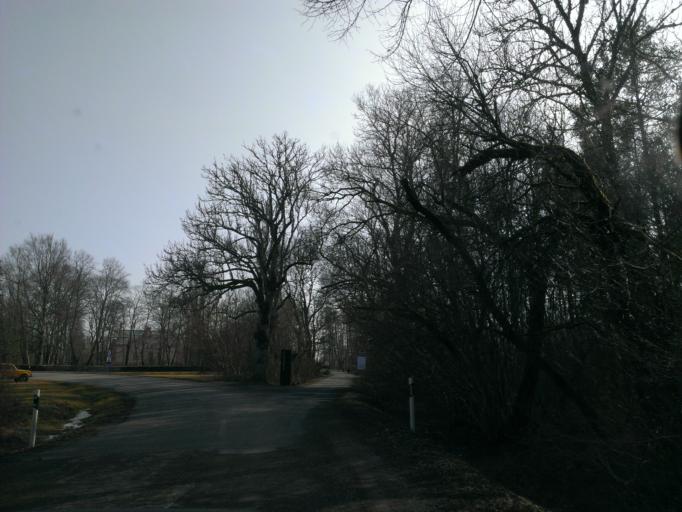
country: EE
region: Saare
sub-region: Orissaare vald
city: Orissaare
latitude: 58.5521
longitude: 23.2786
